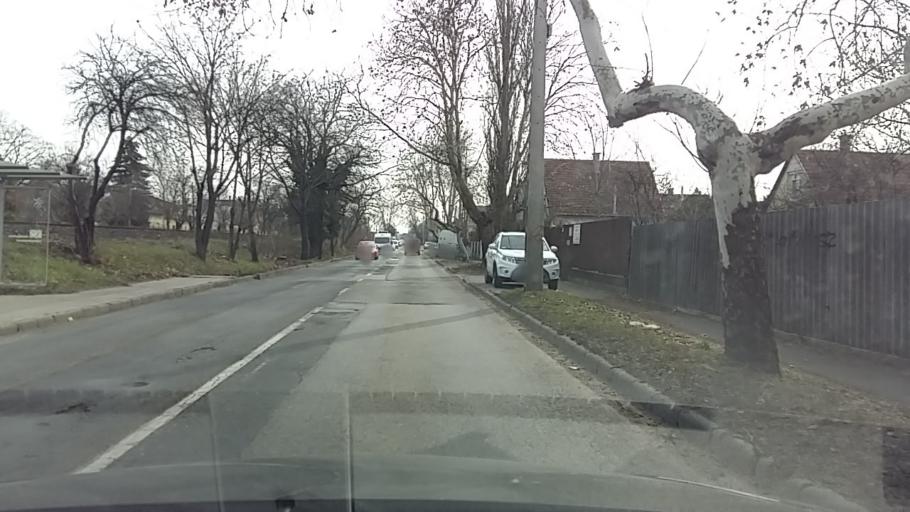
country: HU
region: Budapest
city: Budapest XVIII. keruelet
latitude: 47.4105
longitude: 19.1773
